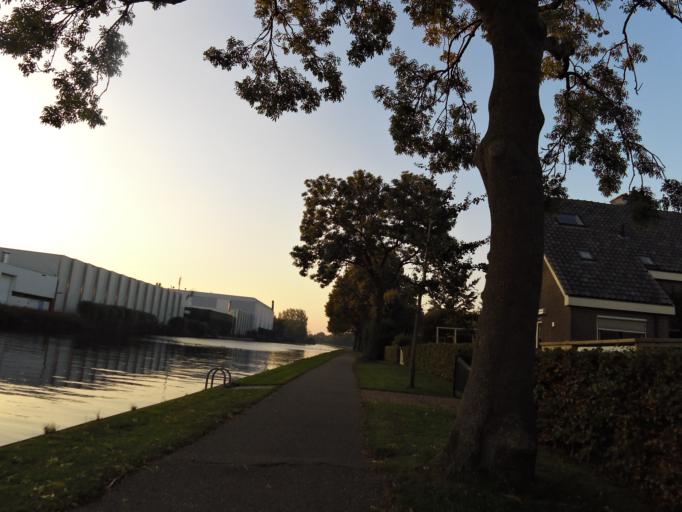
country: NL
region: South Holland
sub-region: Gemeente Leiderdorp
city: Leiderdorp
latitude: 52.1338
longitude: 4.5577
